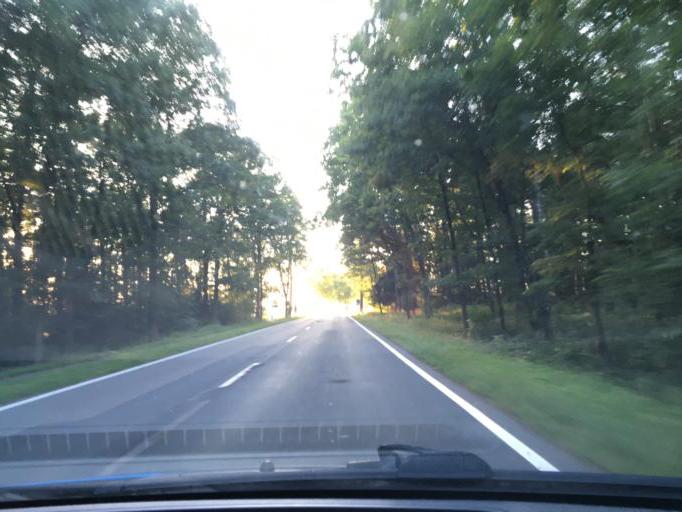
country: DE
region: Lower Saxony
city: Rehlingen
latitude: 53.0901
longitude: 10.2681
